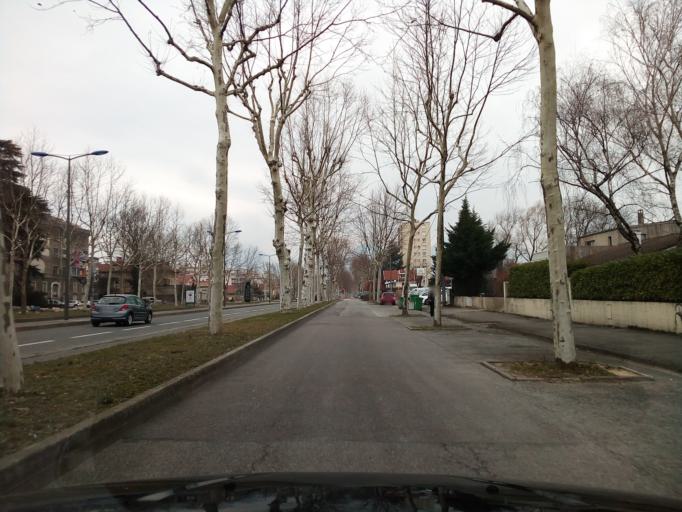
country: FR
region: Rhone-Alpes
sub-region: Departement de l'Isere
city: Le Pont-de-Claix
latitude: 45.1394
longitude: 5.7029
